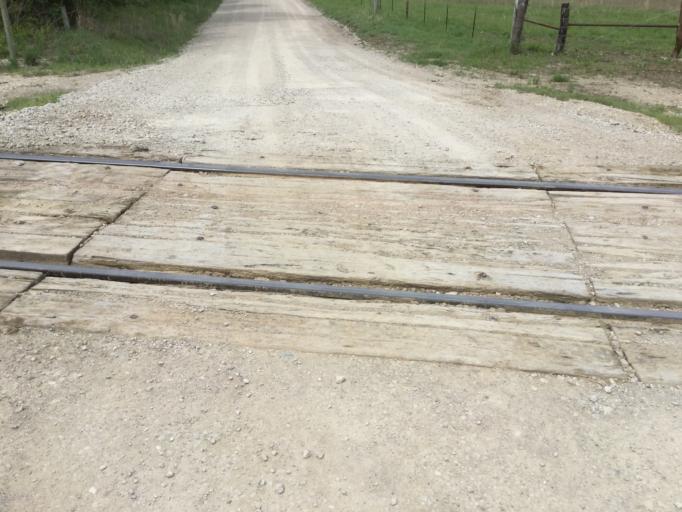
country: US
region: Kansas
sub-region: Montgomery County
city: Cherryvale
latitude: 37.2637
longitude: -95.6021
